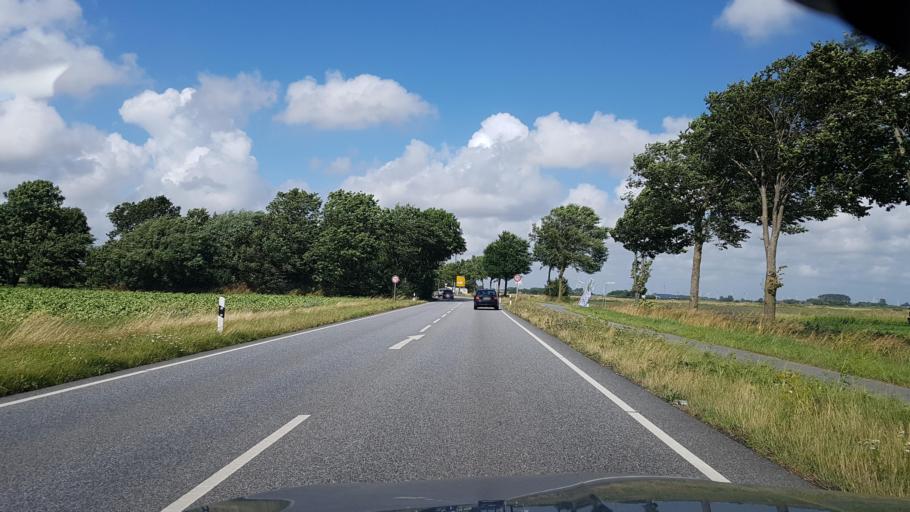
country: DE
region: Schleswig-Holstein
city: Oesterdeichstrich
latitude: 54.1437
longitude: 8.8763
